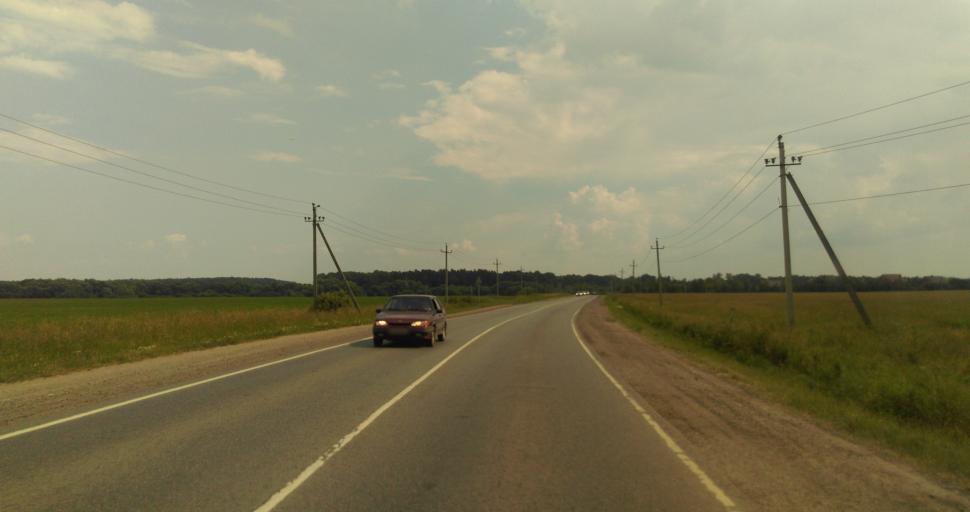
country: RU
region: Moskovskaya
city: Zhitnevo
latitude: 55.3743
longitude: 37.8903
